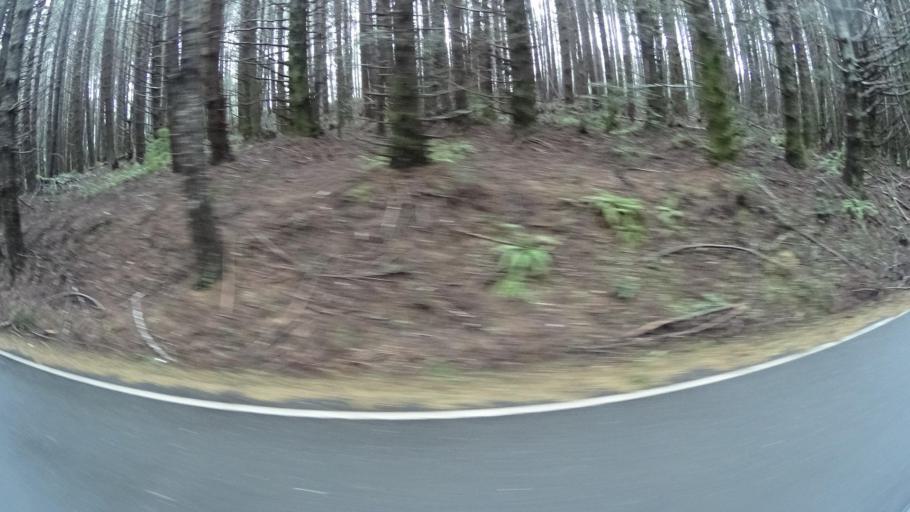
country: US
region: California
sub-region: Humboldt County
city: Westhaven-Moonstone
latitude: 41.2158
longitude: -123.9572
